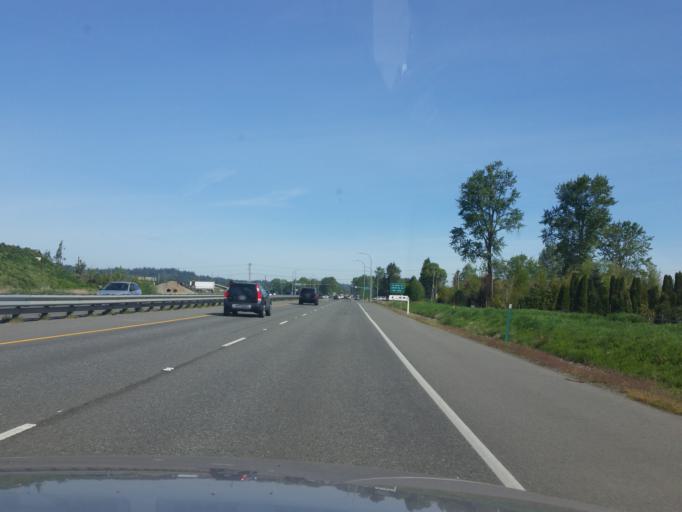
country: US
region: Washington
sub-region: Snohomish County
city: Snohomish
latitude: 47.8958
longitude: -122.1094
